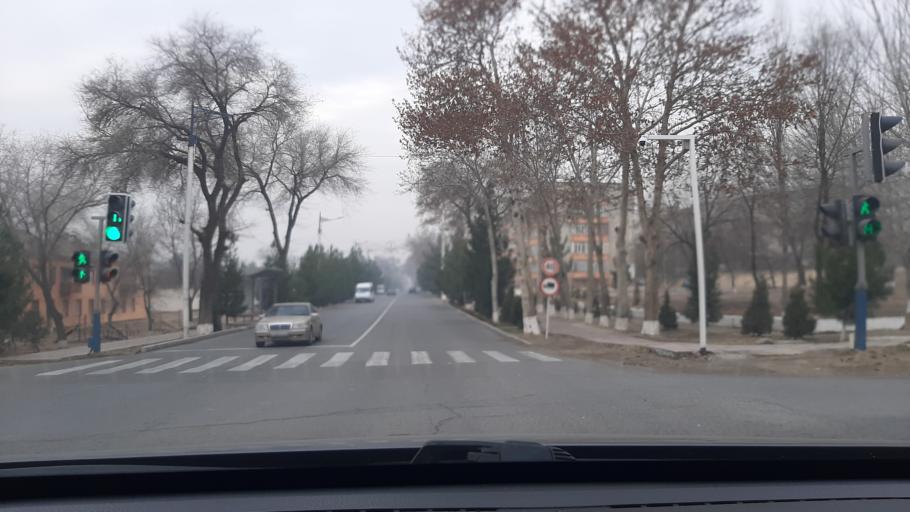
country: TJ
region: Viloyati Sughd
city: Palos
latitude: 40.2691
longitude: 69.8077
